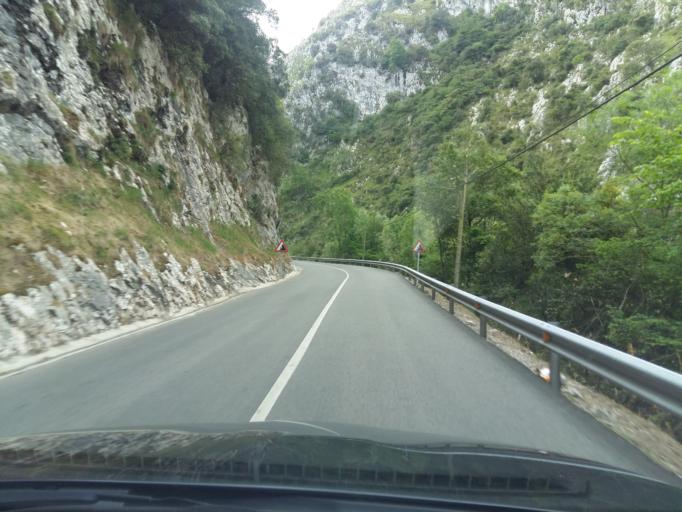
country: ES
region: Cantabria
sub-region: Provincia de Cantabria
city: Tresviso
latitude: 43.3086
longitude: -4.6077
